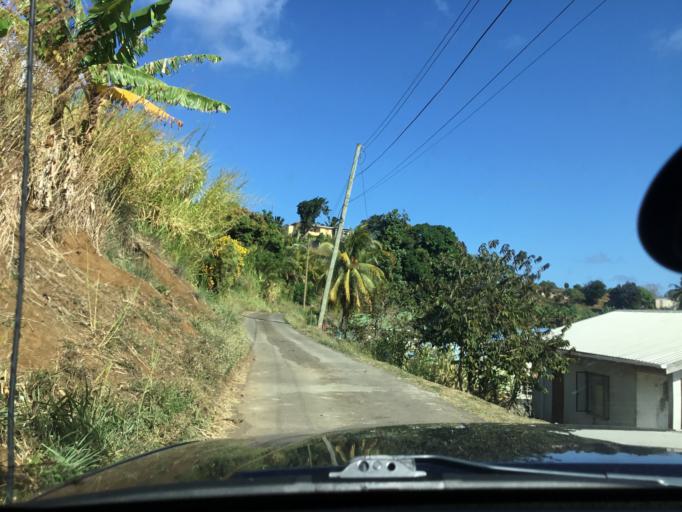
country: VC
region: Charlotte
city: Biabou
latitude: 13.1604
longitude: -61.1635
